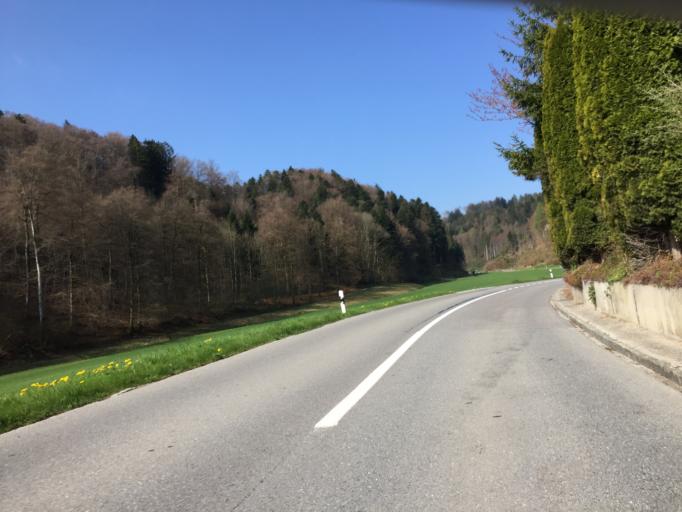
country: CH
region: Bern
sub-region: Bern-Mittelland District
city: Bariswil
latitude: 46.9986
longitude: 7.5330
